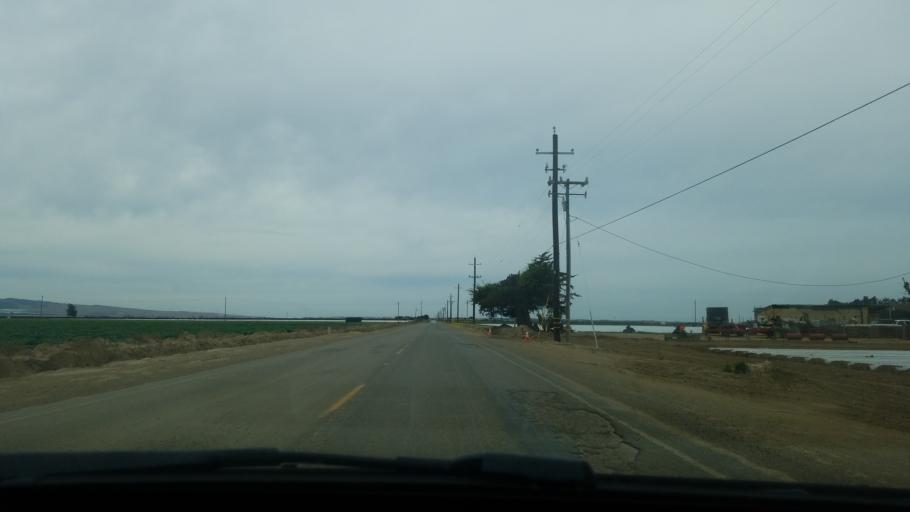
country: US
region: California
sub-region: San Luis Obispo County
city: Nipomo
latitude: 35.0058
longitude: -120.5067
